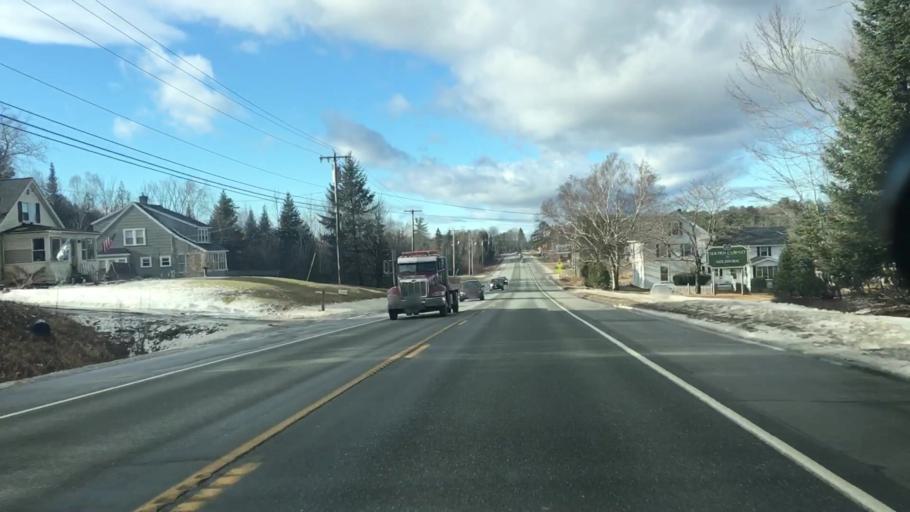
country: US
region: Maine
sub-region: Penobscot County
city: Holden
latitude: 44.7521
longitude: -68.6547
